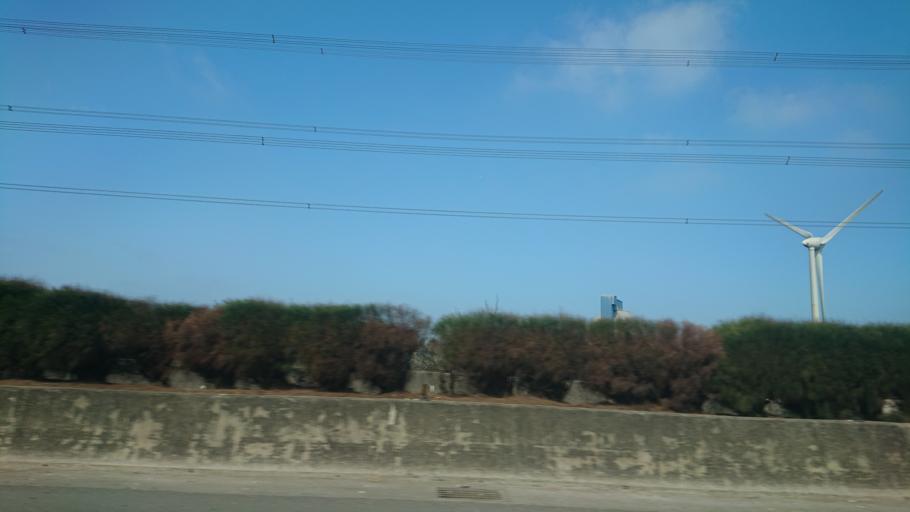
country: TW
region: Taiwan
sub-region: Changhua
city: Chang-hua
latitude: 24.1489
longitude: 120.4523
